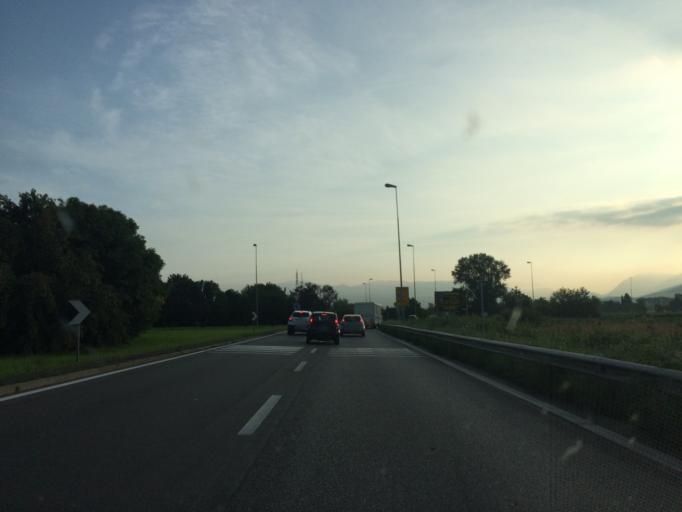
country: IT
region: Lombardy
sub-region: Provincia di Brescia
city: Castel Mella
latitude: 45.5066
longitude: 10.1660
